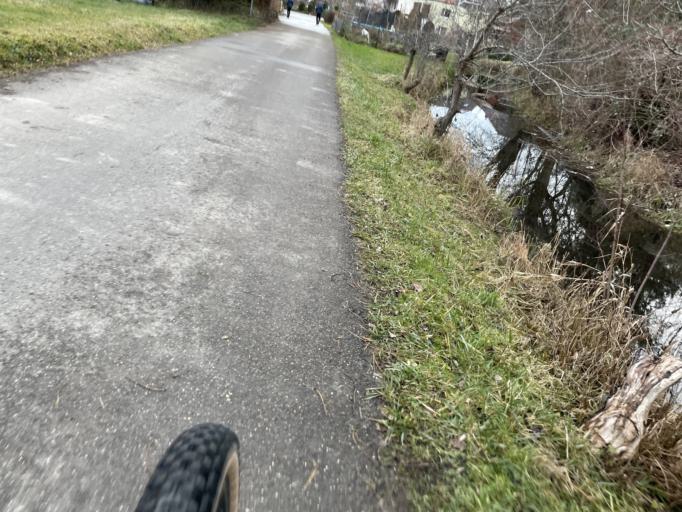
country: CH
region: Bern
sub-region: Bern-Mittelland District
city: Munsingen
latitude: 46.8754
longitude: 7.5468
